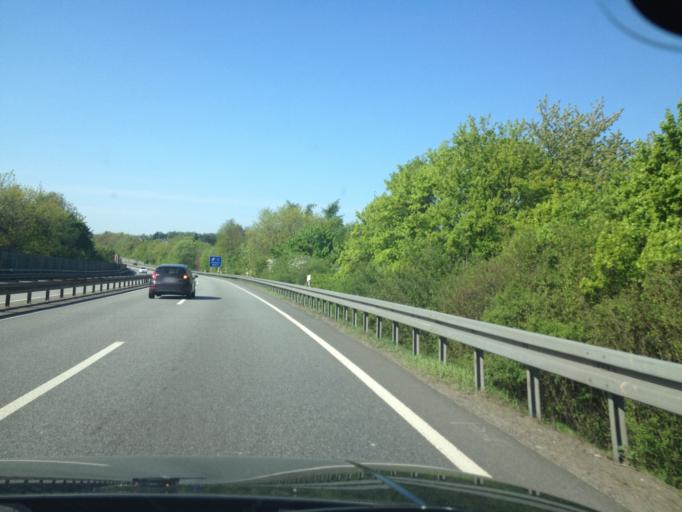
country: DE
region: Saarland
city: Sulzbach
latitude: 49.3128
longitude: 7.0664
